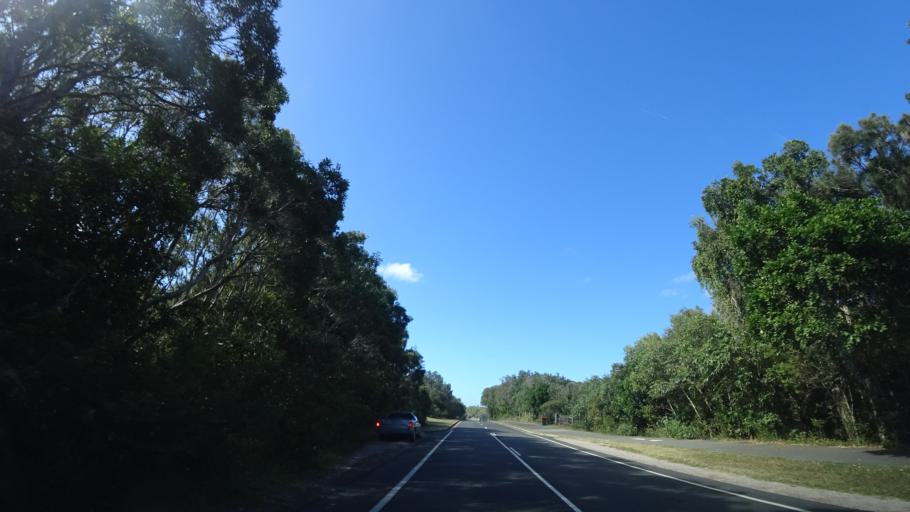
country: AU
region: Queensland
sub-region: Sunshine Coast
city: Mooloolaba
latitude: -26.6207
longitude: 153.1006
